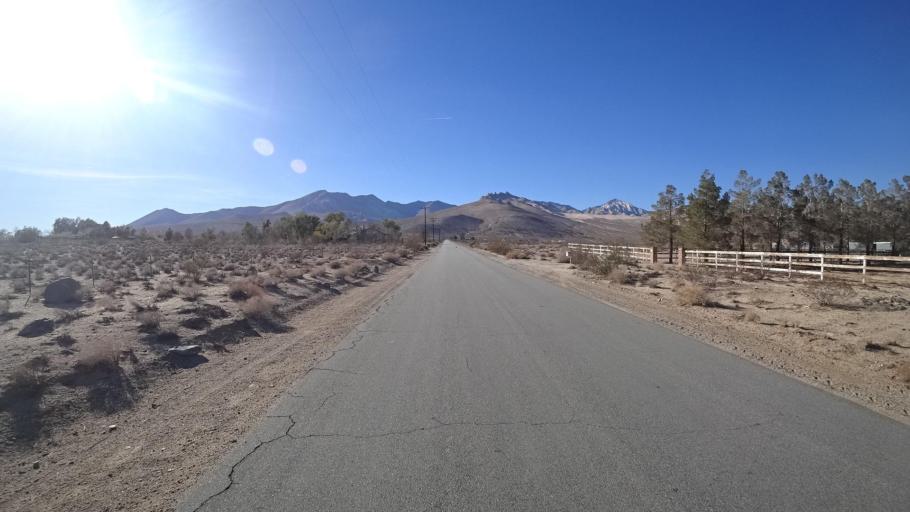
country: US
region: California
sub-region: Kern County
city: Inyokern
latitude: 35.6812
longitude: -117.8517
